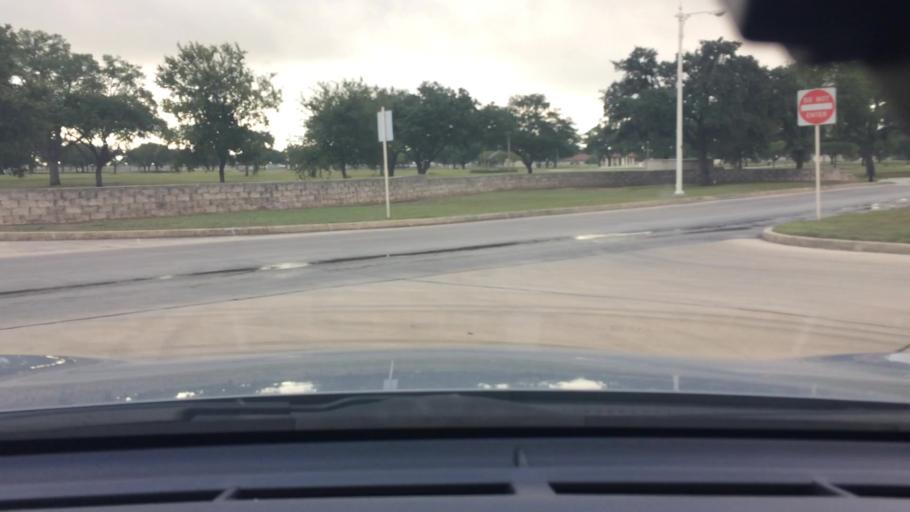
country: US
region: Texas
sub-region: Bexar County
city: Universal City
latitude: 29.5422
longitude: -98.2869
